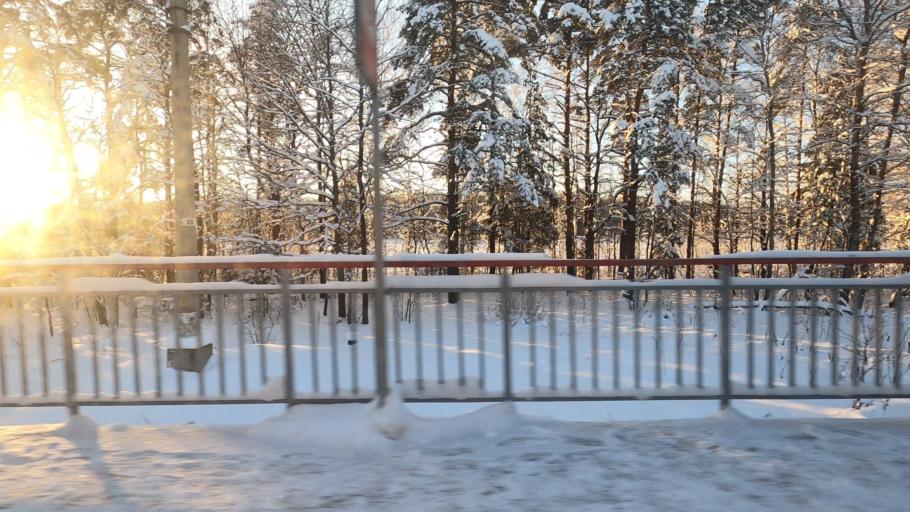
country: RU
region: Moskovskaya
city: Novo-Nikol'skoye
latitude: 56.6379
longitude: 37.5619
